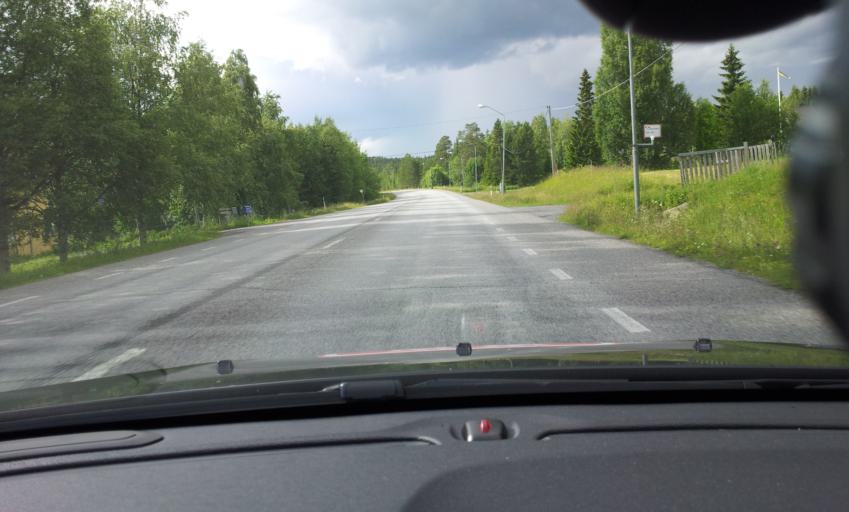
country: SE
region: Jaemtland
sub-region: Are Kommun
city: Jarpen
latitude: 63.3334
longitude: 13.5203
